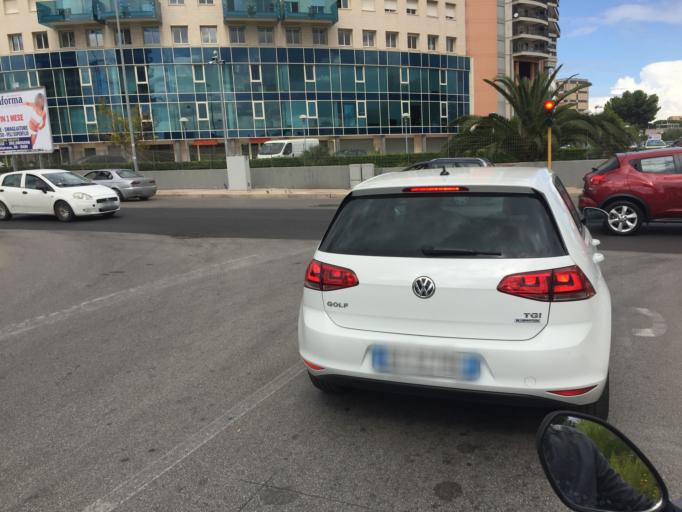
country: IT
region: Apulia
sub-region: Provincia di Bari
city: Bari
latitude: 41.1075
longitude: 16.8534
